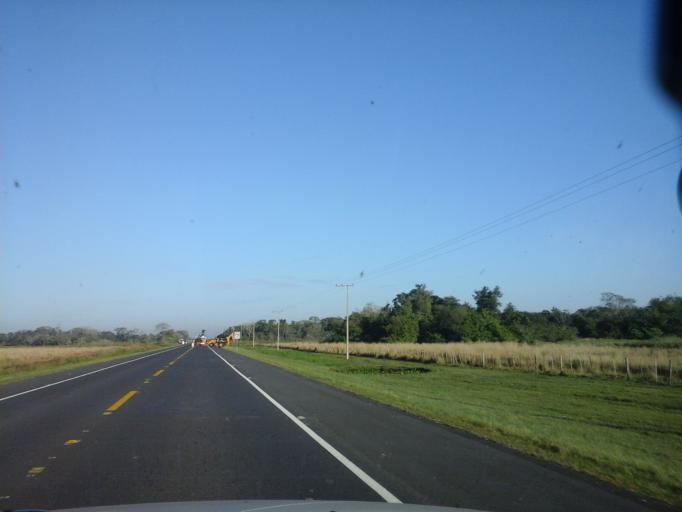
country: PY
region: Neembucu
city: Pilar
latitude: -26.8556
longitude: -57.9712
